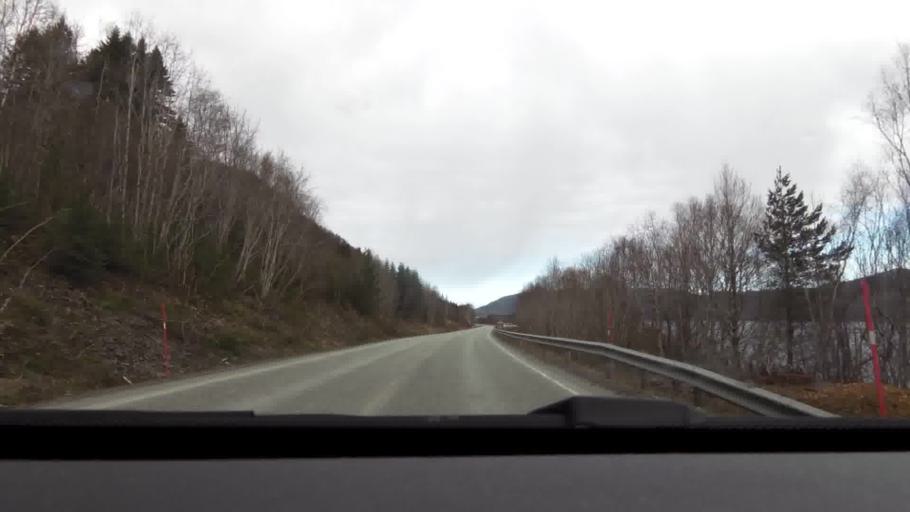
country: NO
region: More og Romsdal
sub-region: Eide
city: Eide
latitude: 62.9366
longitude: 7.4344
